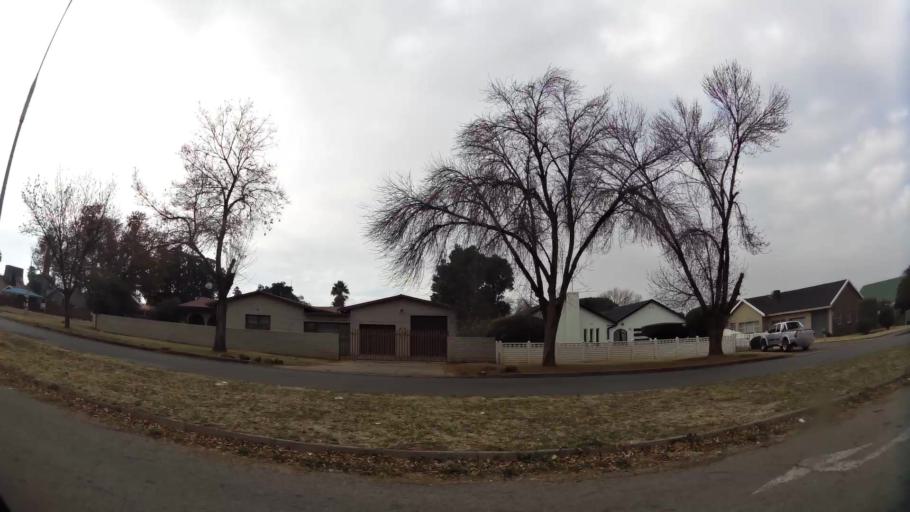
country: ZA
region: Gauteng
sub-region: Sedibeng District Municipality
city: Vanderbijlpark
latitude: -26.6985
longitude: 27.8476
